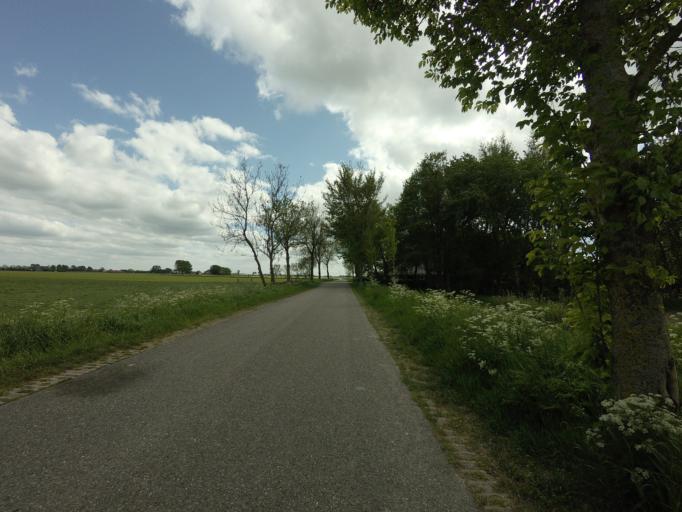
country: NL
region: Friesland
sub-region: Sudwest Fryslan
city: Bolsward
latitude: 53.0848
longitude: 5.5481
